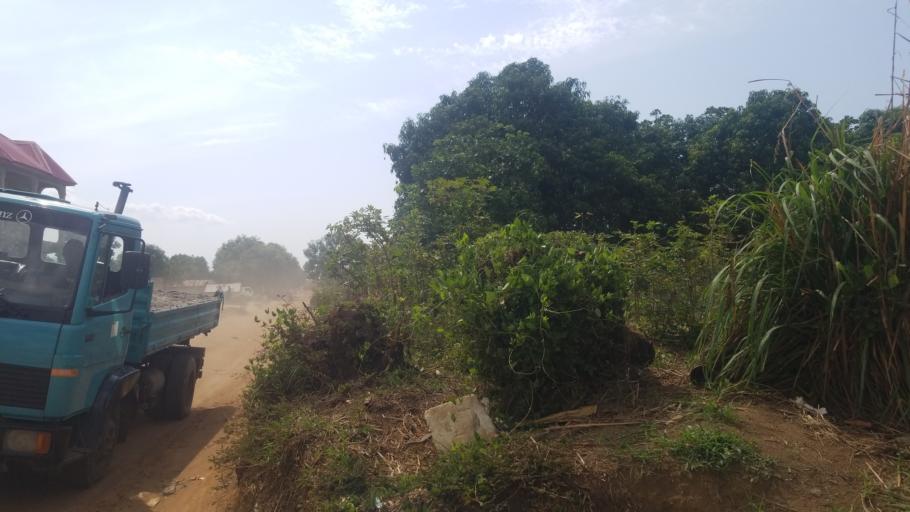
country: SL
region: Western Area
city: Waterloo
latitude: 8.3448
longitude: -13.0496
